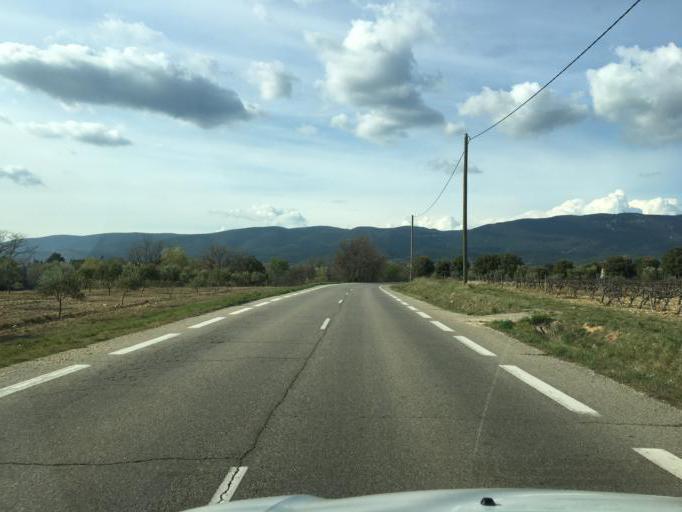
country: FR
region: Provence-Alpes-Cote d'Azur
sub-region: Departement du Vaucluse
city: Ansouis
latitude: 43.7511
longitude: 5.4615
